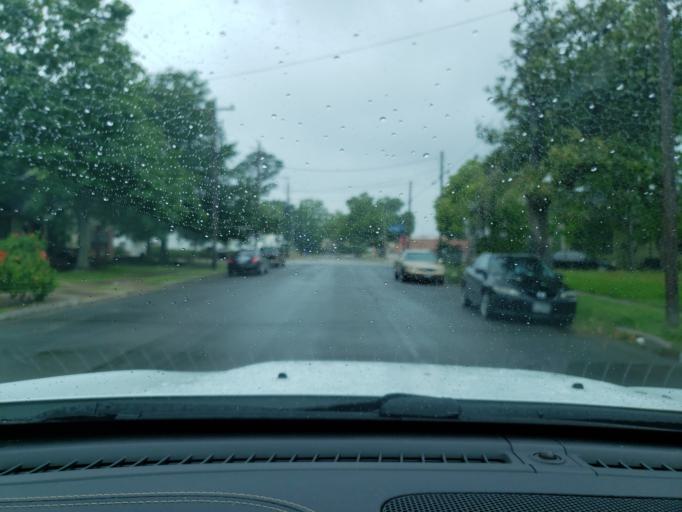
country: US
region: Texas
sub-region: Harris County
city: Baytown
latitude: 29.7333
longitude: -94.9736
